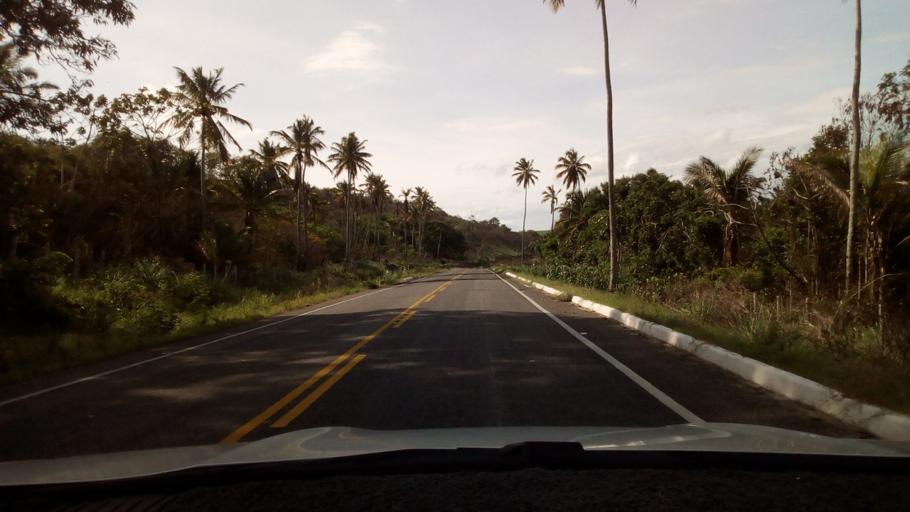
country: BR
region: Paraiba
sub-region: Cabedelo
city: Cabedelo
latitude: -7.0099
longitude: -34.8812
